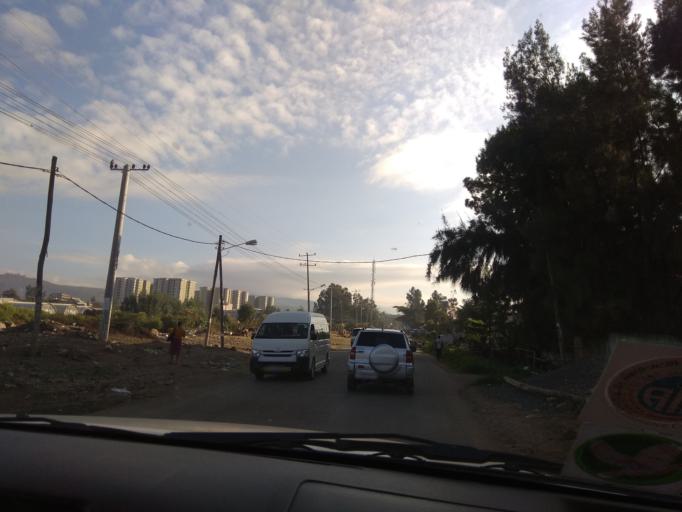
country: ET
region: Adis Abeba
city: Addis Ababa
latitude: 8.9949
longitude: 38.8041
